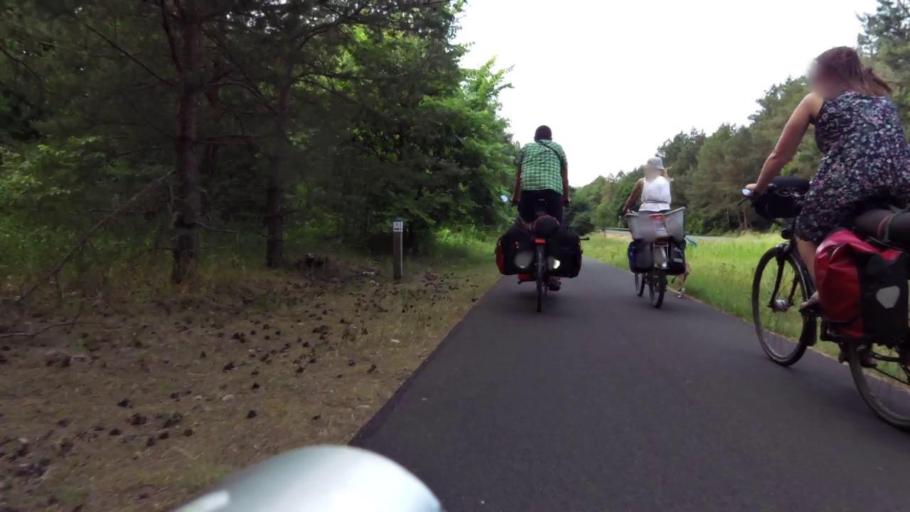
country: PL
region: Kujawsko-Pomorskie
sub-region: Powiat torunski
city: Lysomice
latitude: 53.0785
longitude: 18.5410
